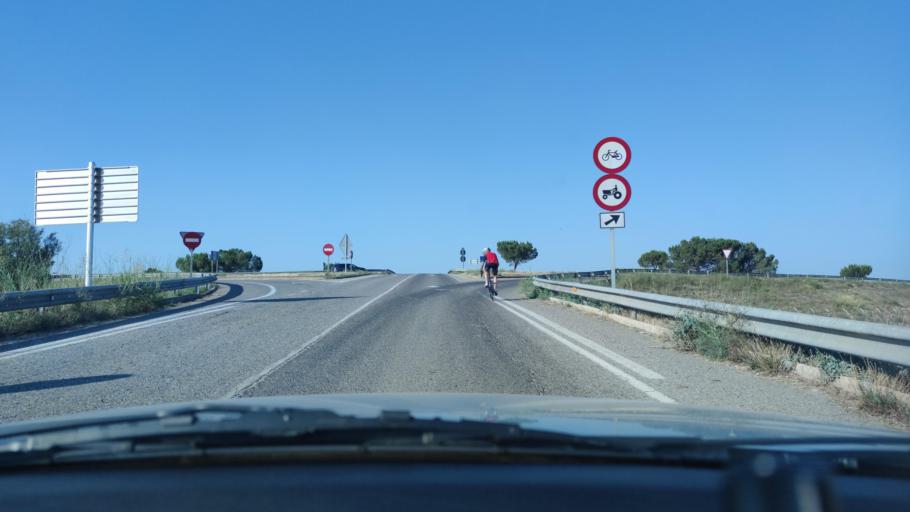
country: ES
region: Catalonia
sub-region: Provincia de Lleida
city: Sidamon
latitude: 41.6377
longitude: 0.7909
